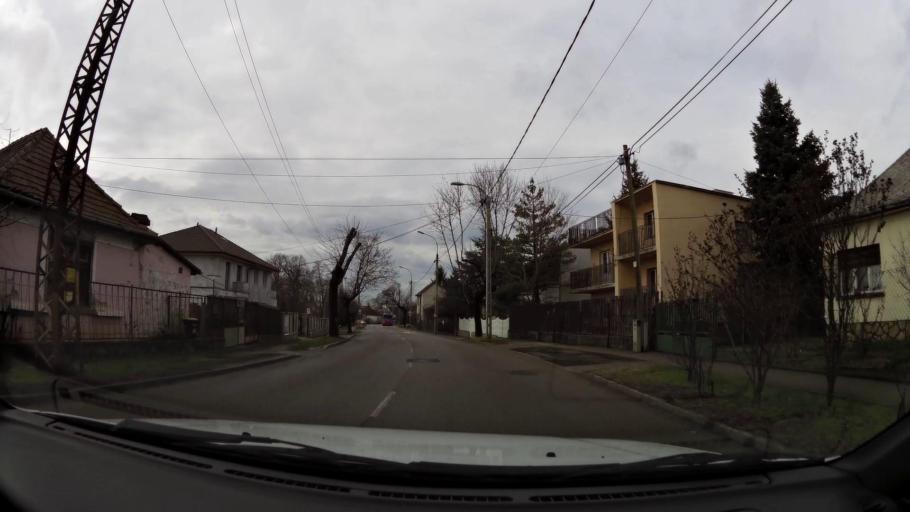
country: HU
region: Budapest
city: Budapest XVII. keruelet
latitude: 47.4964
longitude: 19.2619
